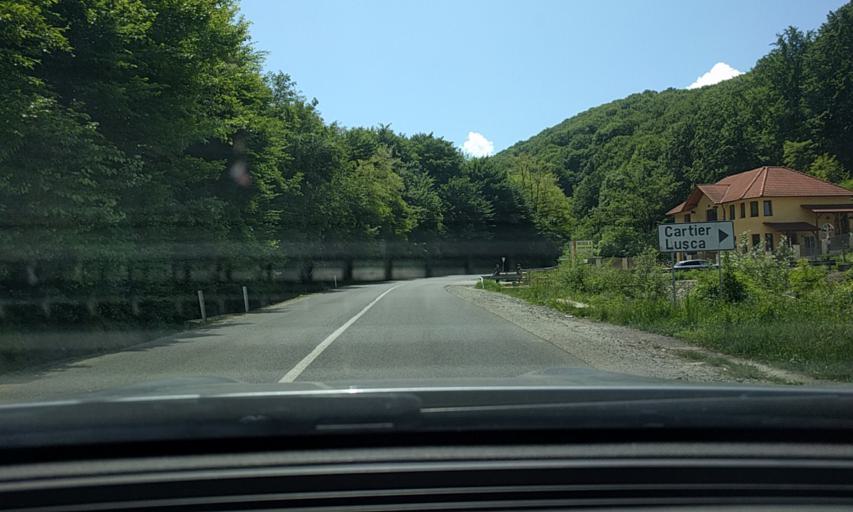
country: RO
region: Bistrita-Nasaud
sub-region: Oras Nasaud
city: Nasaud
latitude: 47.2774
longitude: 24.4223
